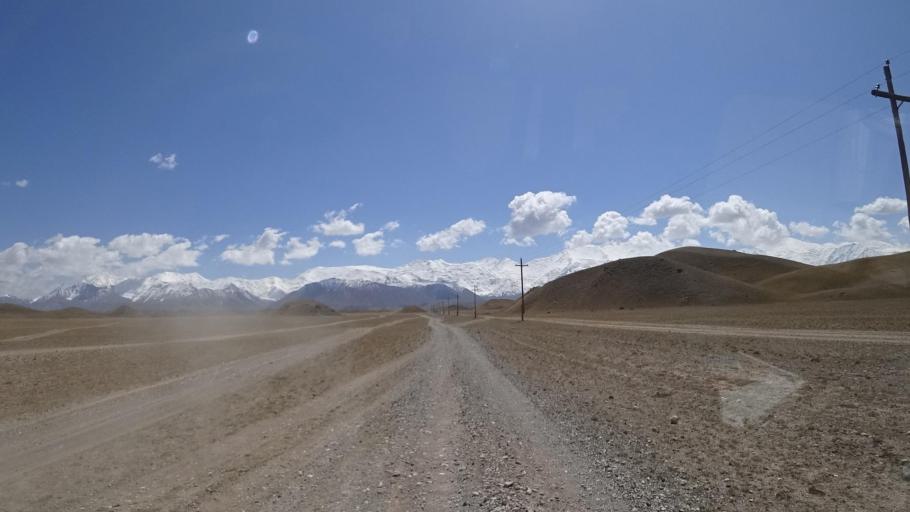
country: KG
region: Osh
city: Gul'cha
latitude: 39.5960
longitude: 72.8840
